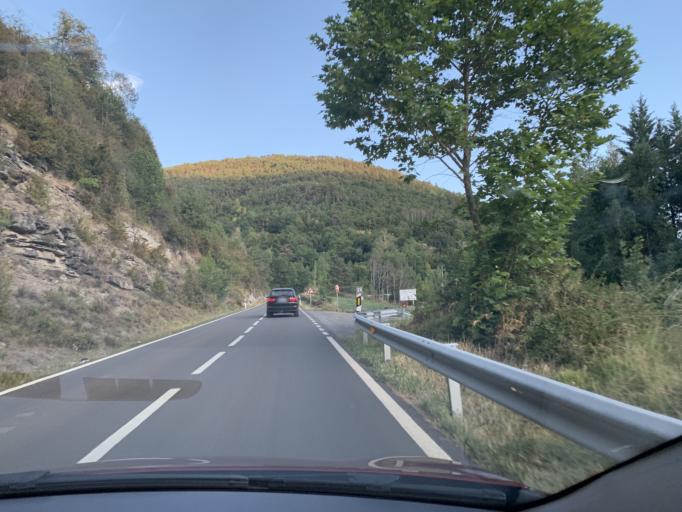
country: ES
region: Aragon
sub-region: Provincia de Huesca
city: Broto
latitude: 42.5992
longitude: -0.1184
